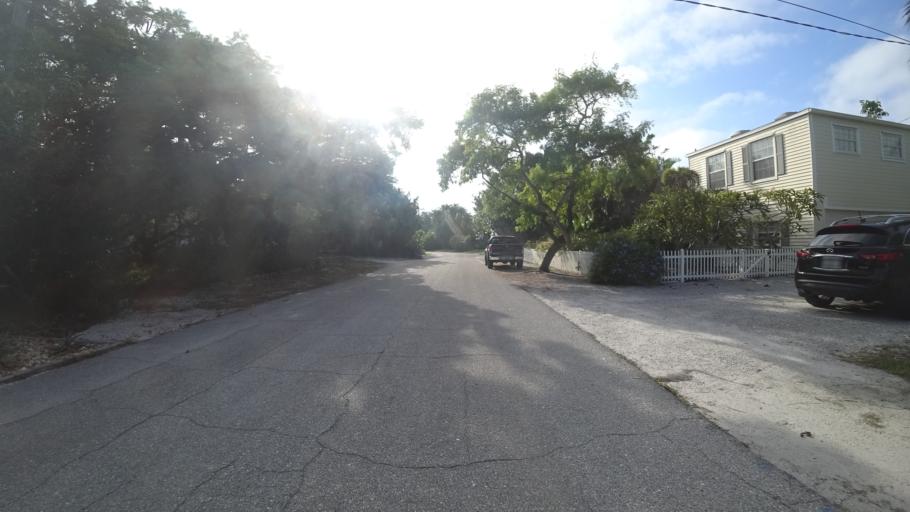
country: US
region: Florida
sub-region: Manatee County
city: Longboat Key
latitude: 27.4355
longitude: -82.6817
